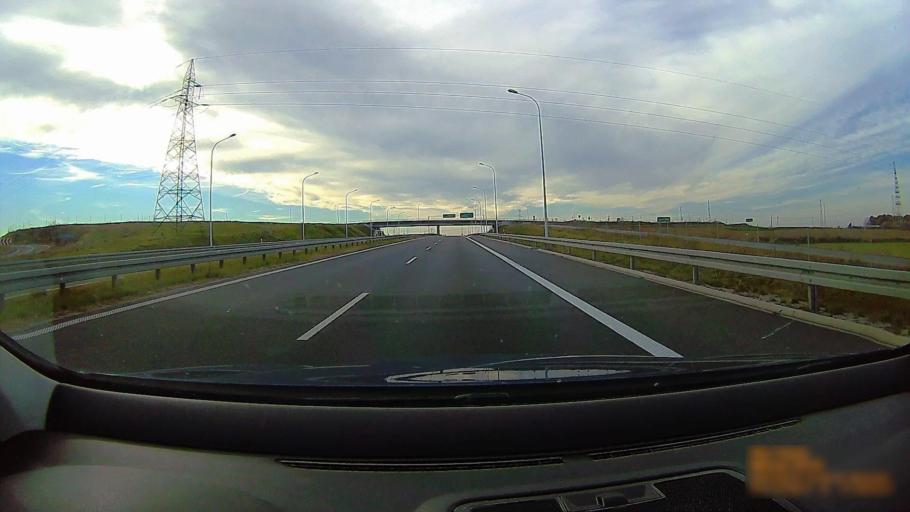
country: PL
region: Greater Poland Voivodeship
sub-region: Powiat ostrowski
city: Przygodzice
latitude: 51.6324
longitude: 17.8703
